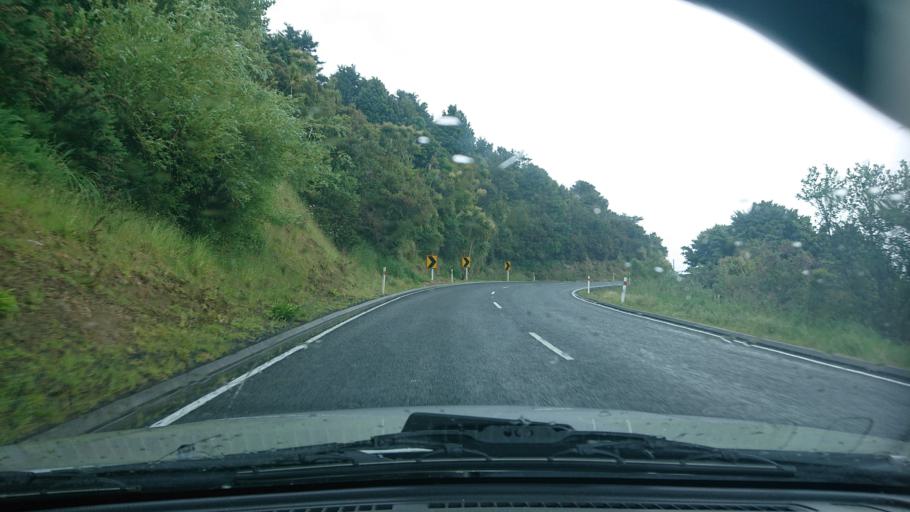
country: NZ
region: Auckland
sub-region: Auckland
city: Wellsford
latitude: -36.3490
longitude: 174.4743
